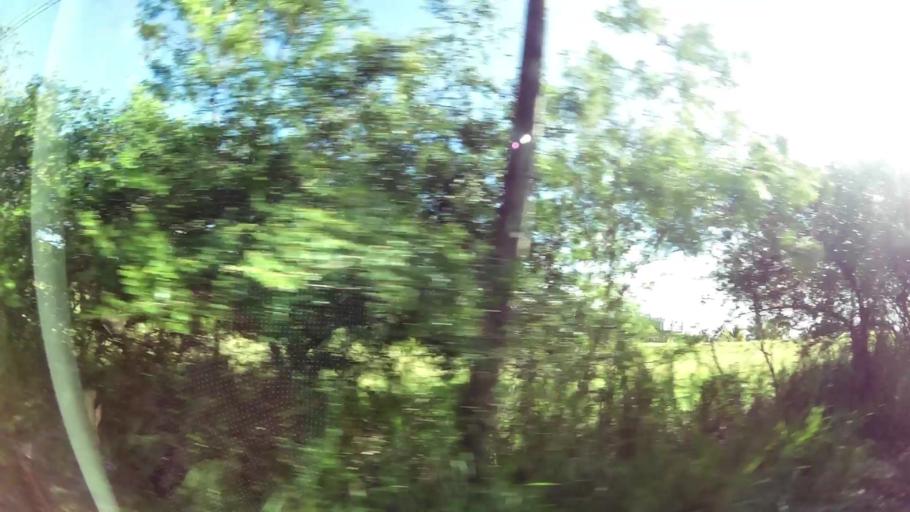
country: GP
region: Guadeloupe
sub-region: Guadeloupe
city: Petit-Canal
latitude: 16.3685
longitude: -61.4653
